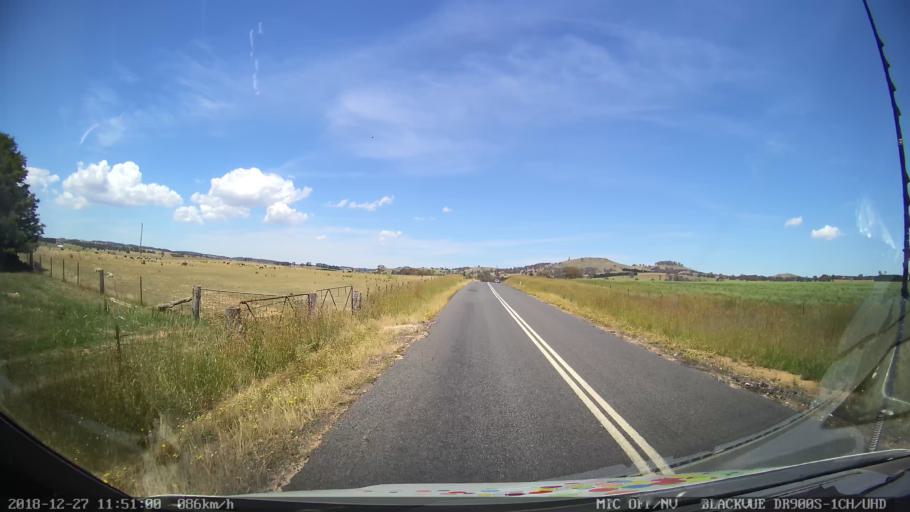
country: AU
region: New South Wales
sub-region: Bathurst Regional
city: Perthville
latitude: -33.6370
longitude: 149.4262
